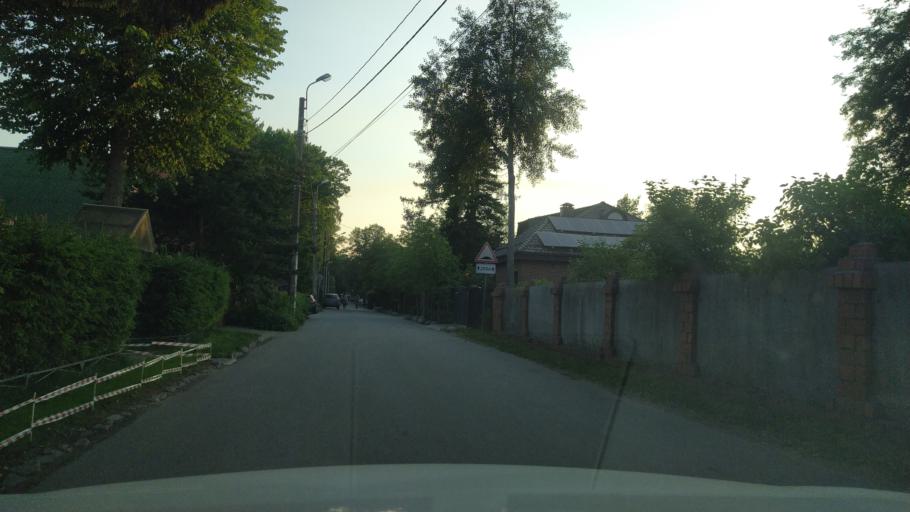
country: RU
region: St.-Petersburg
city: Sestroretsk
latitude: 60.0929
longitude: 29.9471
